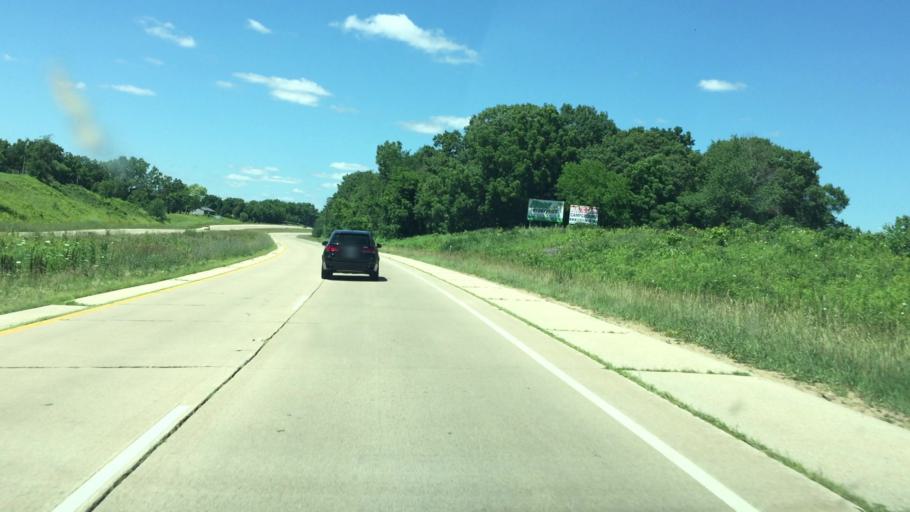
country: US
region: Illinois
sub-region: Jo Daviess County
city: East Dubuque
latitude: 42.5457
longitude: -90.6075
